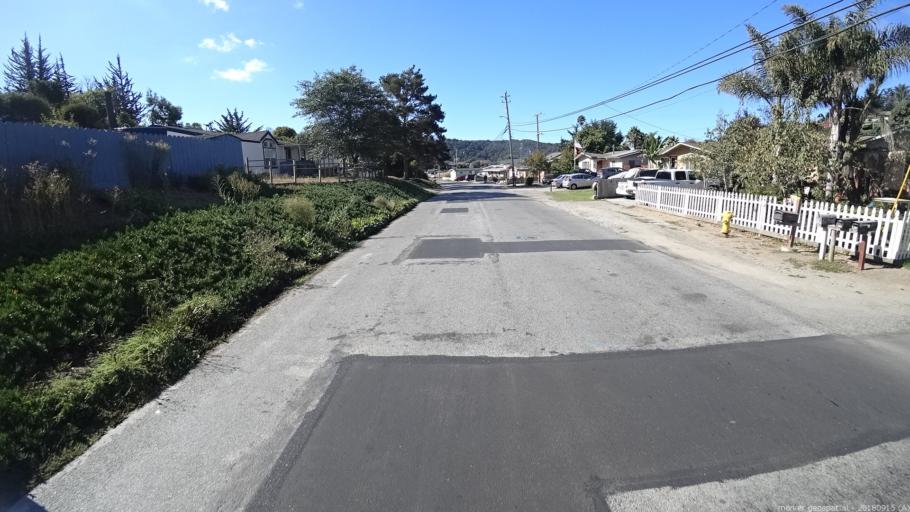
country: US
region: California
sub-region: Monterey County
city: Las Lomas
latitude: 36.8669
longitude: -121.7332
